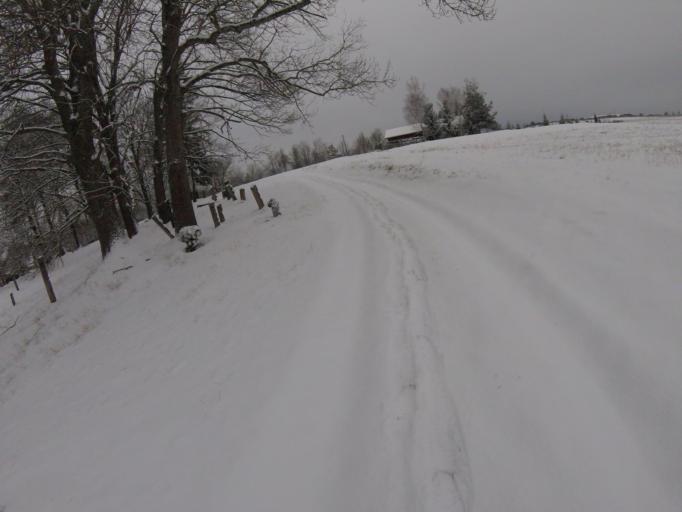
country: HU
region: Borsod-Abauj-Zemplen
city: Rudabanya
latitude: 48.4436
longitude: 20.6336
